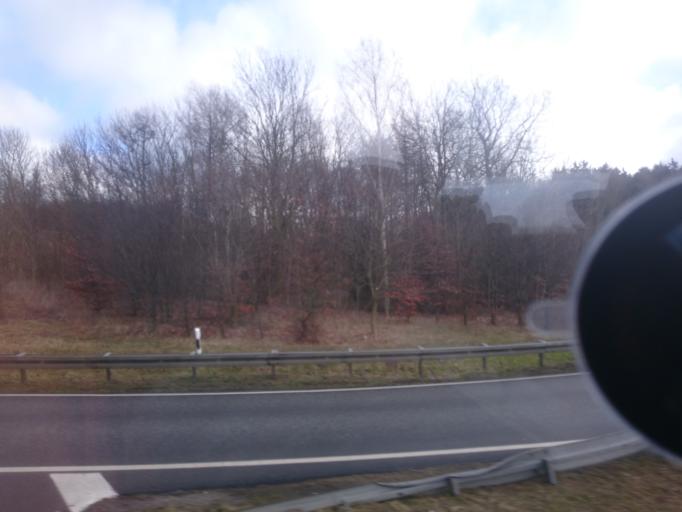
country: DE
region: Mecklenburg-Vorpommern
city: Kavelstorf
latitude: 54.0273
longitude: 12.2007
